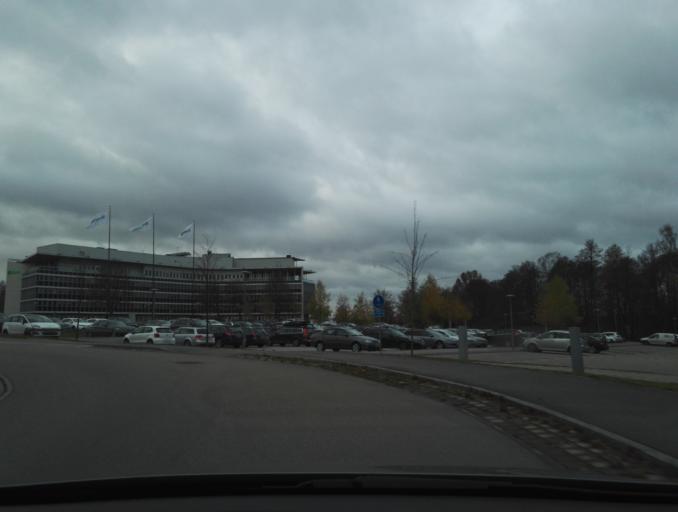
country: SE
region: Kronoberg
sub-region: Vaxjo Kommun
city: Vaexjoe
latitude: 56.8607
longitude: 14.8173
